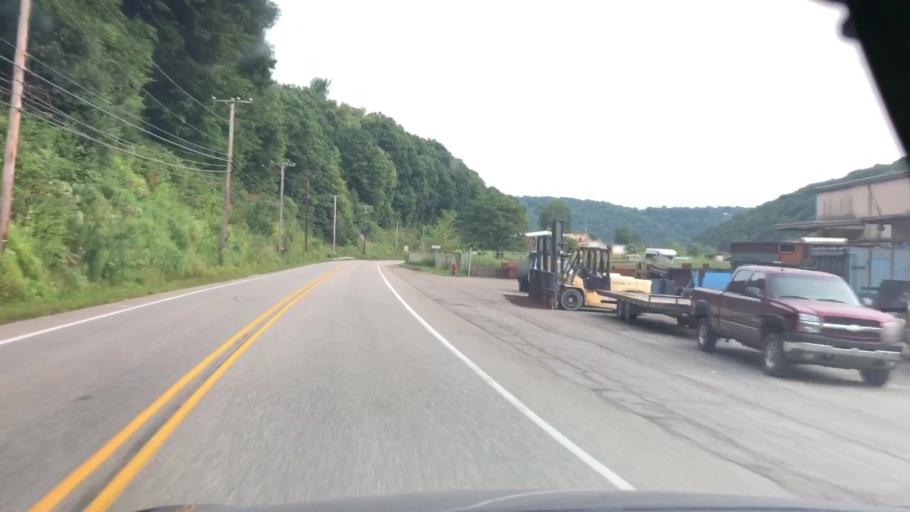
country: US
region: Pennsylvania
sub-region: Venango County
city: Hasson Heights
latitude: 41.4641
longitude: -79.6896
